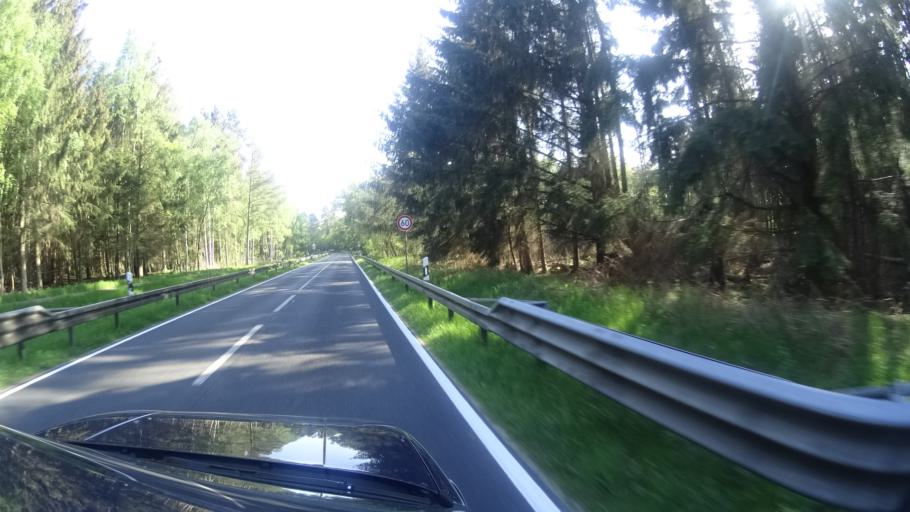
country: DE
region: Mecklenburg-Vorpommern
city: Ostseebad Prerow
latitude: 54.4254
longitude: 12.5723
